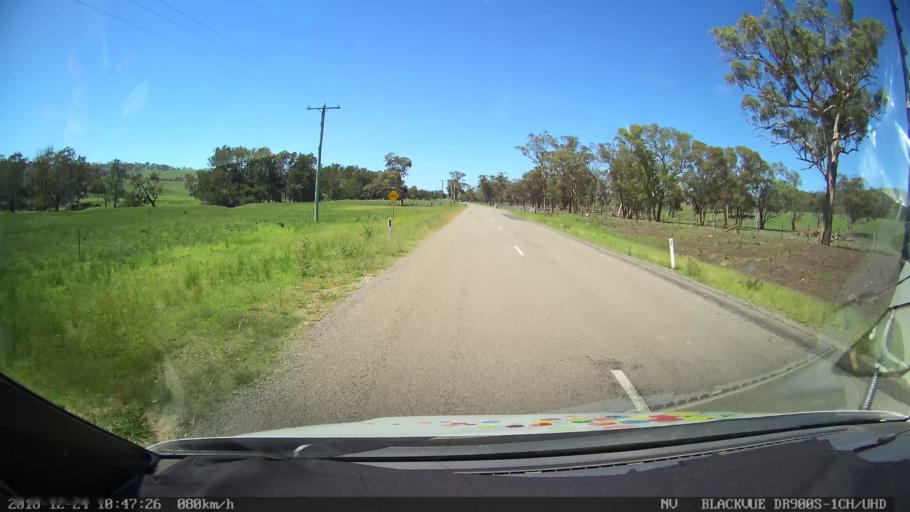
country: AU
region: New South Wales
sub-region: Upper Hunter Shire
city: Merriwa
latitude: -31.9244
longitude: 150.4296
